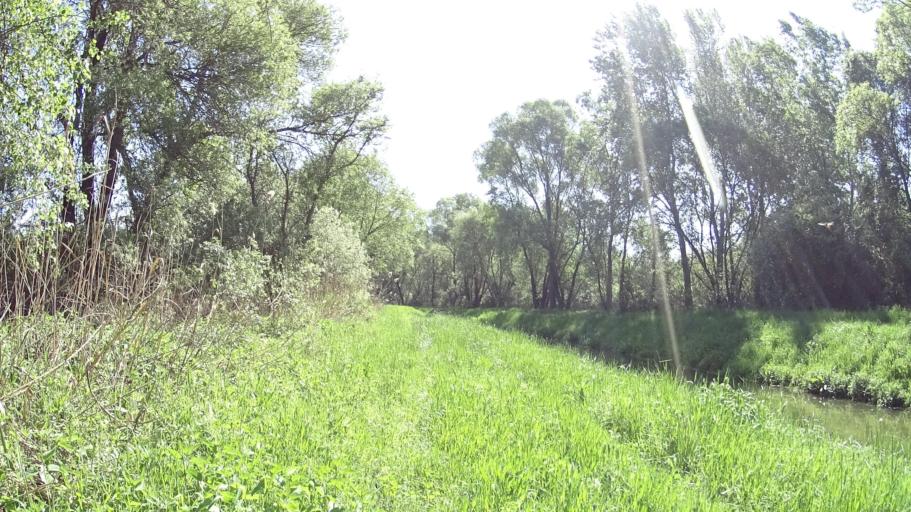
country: HU
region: Pest
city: Gyal
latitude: 47.3718
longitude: 19.1843
